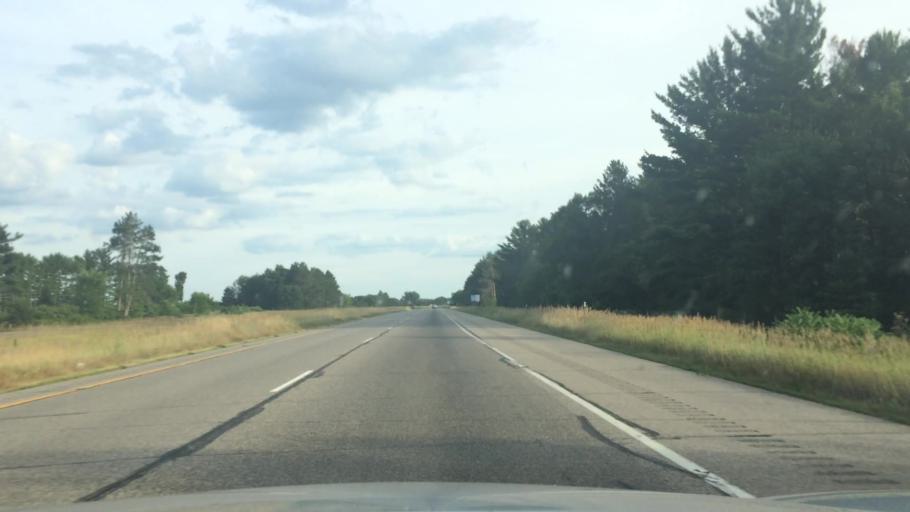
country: US
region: Wisconsin
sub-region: Portage County
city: Plover
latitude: 44.2072
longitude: -89.5240
